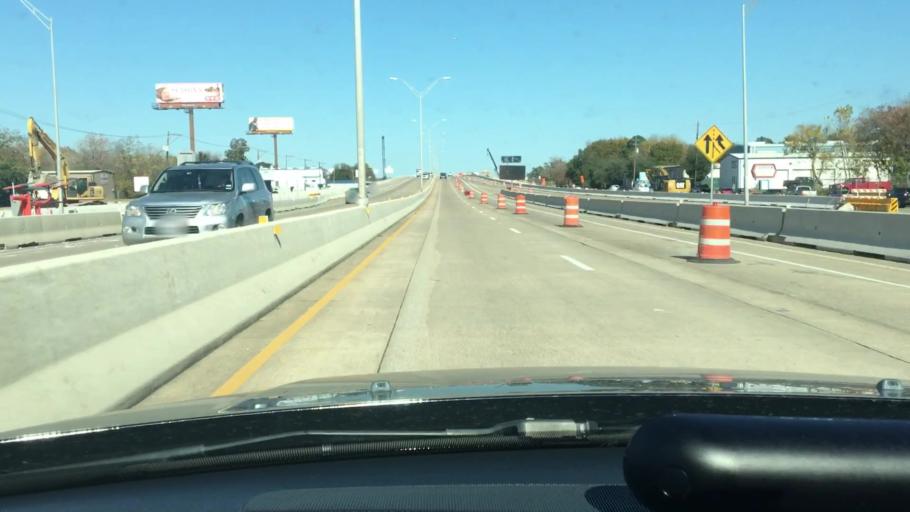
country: US
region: Texas
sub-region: Harris County
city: Deer Park
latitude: 29.6717
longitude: -95.1560
